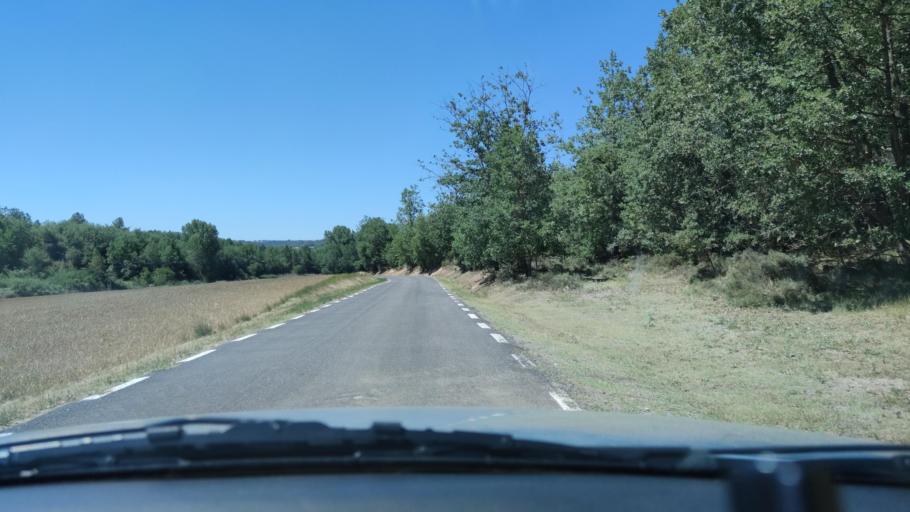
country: ES
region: Catalonia
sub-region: Provincia de Lleida
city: Tora de Riubregos
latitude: 41.9064
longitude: 1.4476
